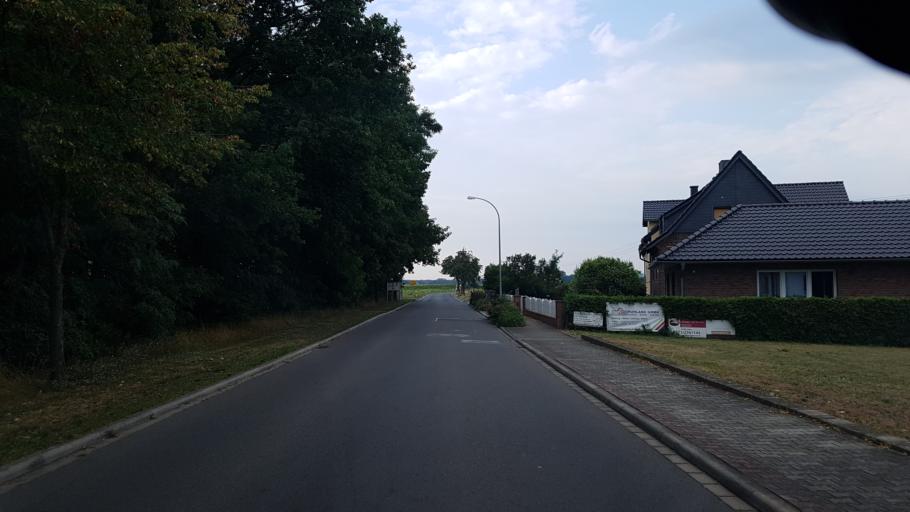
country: DE
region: Brandenburg
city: Tettau
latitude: 51.4240
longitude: 13.7279
